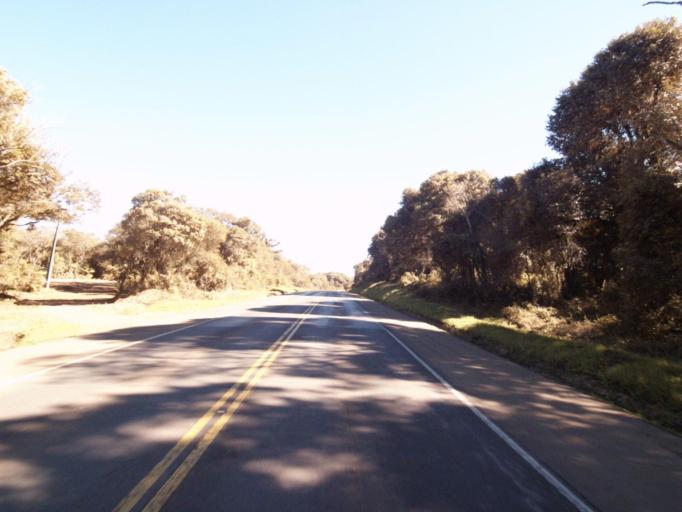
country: BR
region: Santa Catarina
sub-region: Xanxere
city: Xanxere
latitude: -26.8829
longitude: -52.1706
